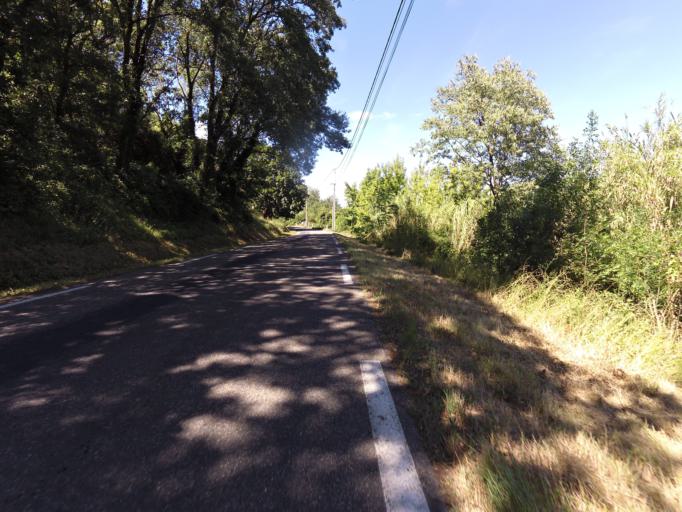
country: FR
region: Languedoc-Roussillon
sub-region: Departement du Gard
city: Sommieres
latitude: 43.8203
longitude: 4.0687
